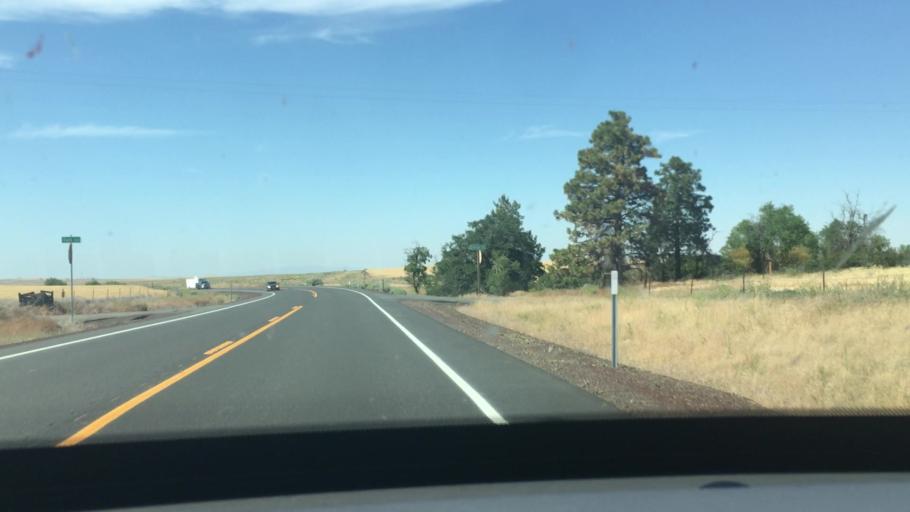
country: US
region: Oregon
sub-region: Sherman County
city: Moro
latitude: 45.3300
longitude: -120.7687
